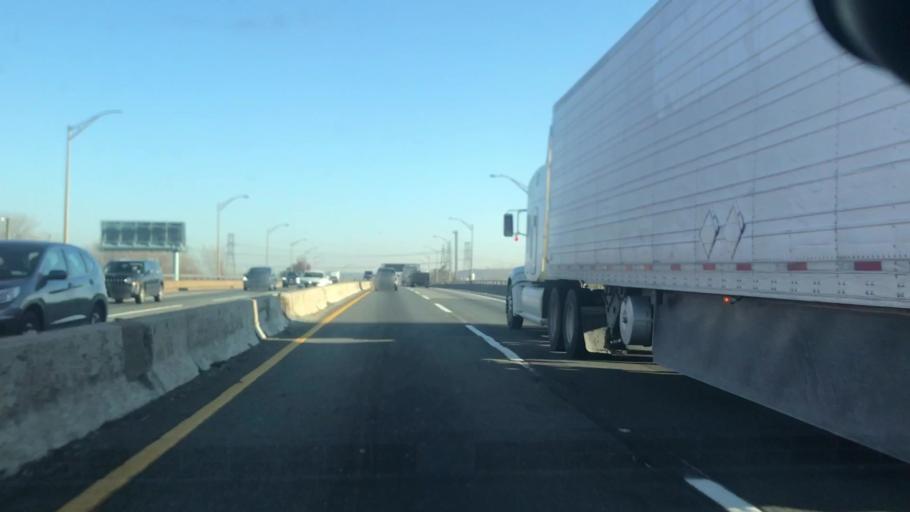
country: US
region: New Jersey
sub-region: Bergen County
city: Ridgefield
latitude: 40.8309
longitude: -74.0250
